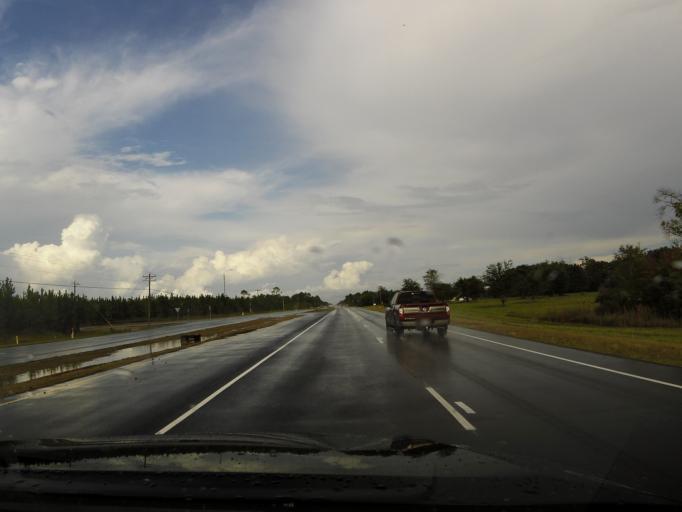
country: US
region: Georgia
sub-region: Long County
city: Ludowici
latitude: 31.7265
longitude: -81.7207
